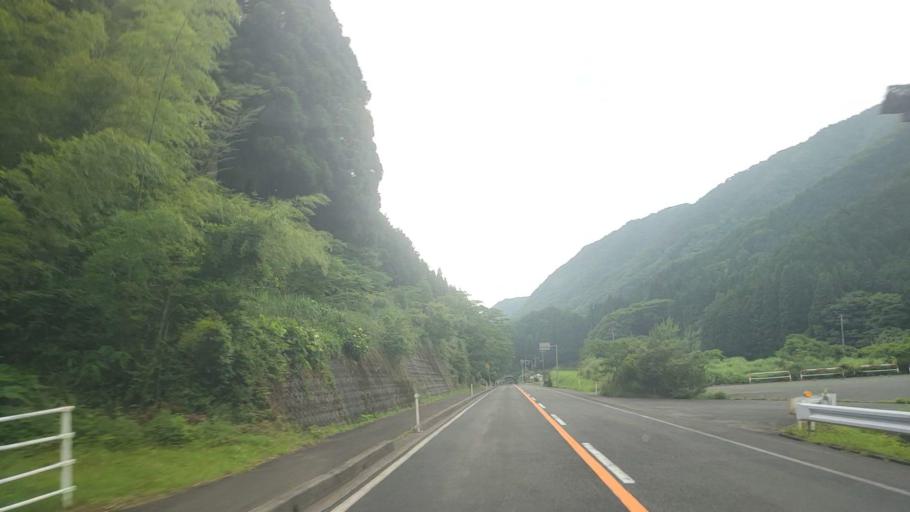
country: JP
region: Tottori
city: Kurayoshi
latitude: 35.3151
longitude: 133.8804
